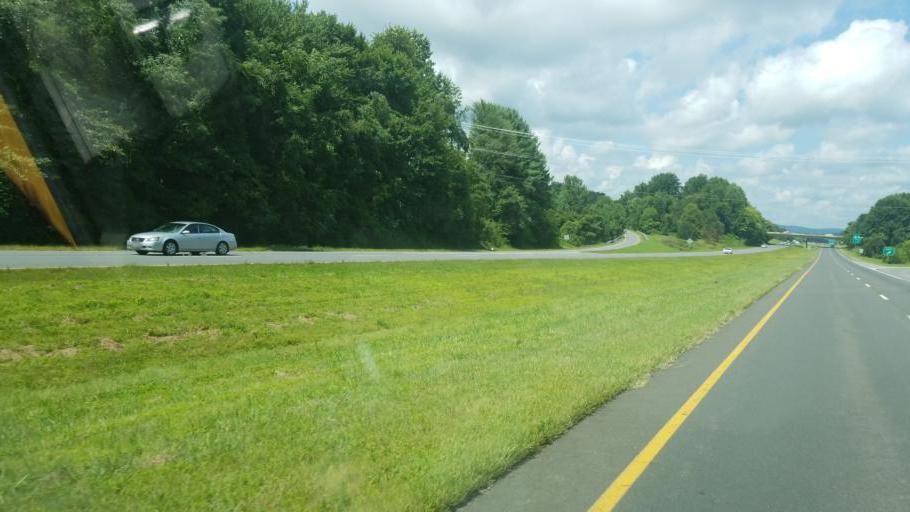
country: US
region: Virginia
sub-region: Fauquier County
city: Warrenton
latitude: 38.7048
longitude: -77.7805
